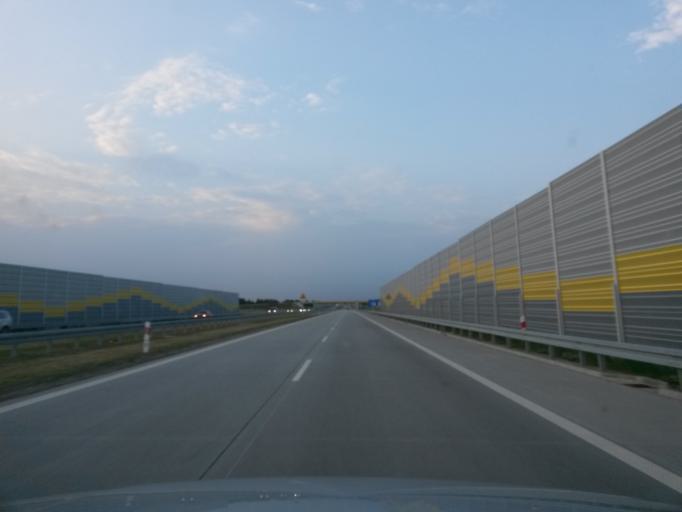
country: PL
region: Lodz Voivodeship
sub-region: Powiat sieradzki
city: Brzeznio
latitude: 51.4815
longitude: 18.6740
